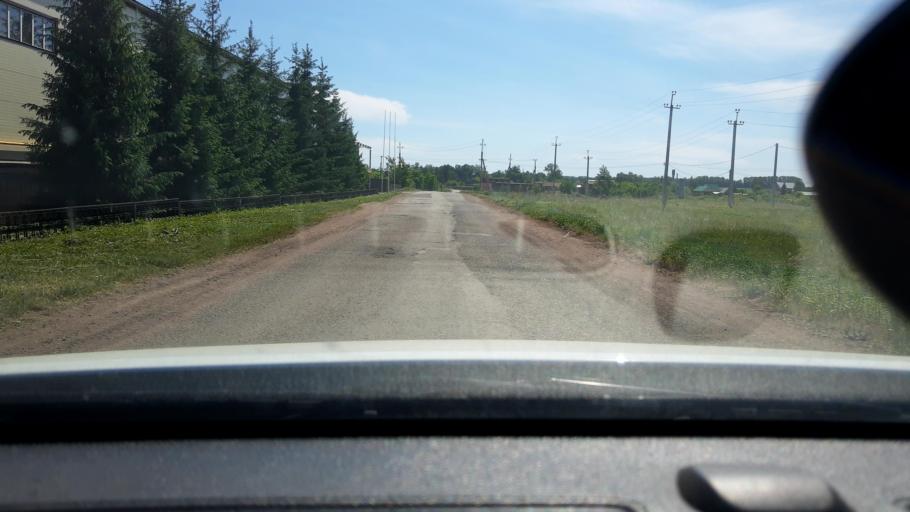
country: RU
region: Bashkortostan
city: Avdon
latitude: 54.5109
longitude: 55.8195
